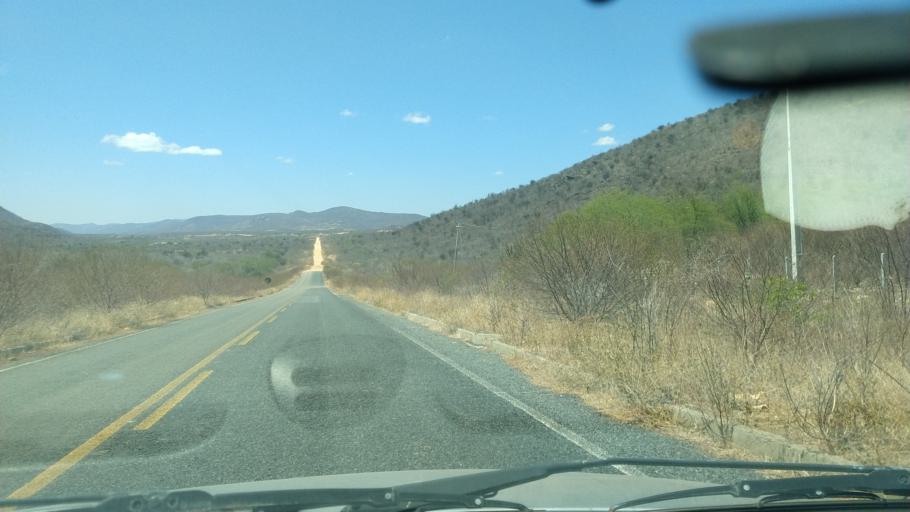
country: BR
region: Rio Grande do Norte
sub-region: Sao Tome
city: Sao Tome
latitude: -5.9675
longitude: -36.1581
